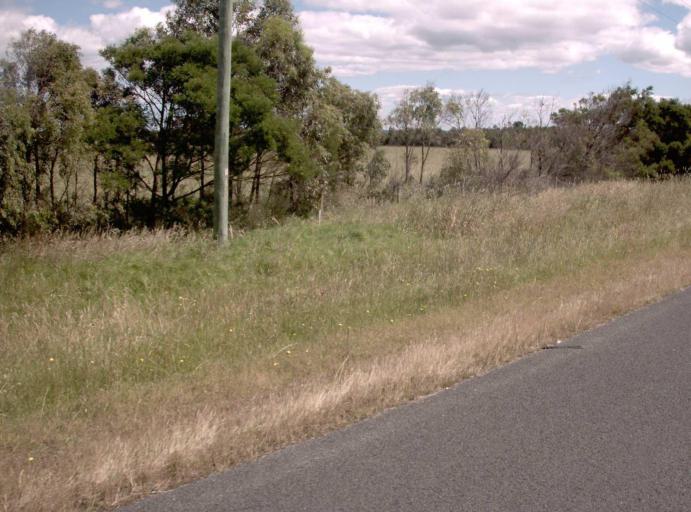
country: AU
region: Victoria
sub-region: Bass Coast
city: North Wonthaggi
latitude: -38.4454
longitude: 145.4825
